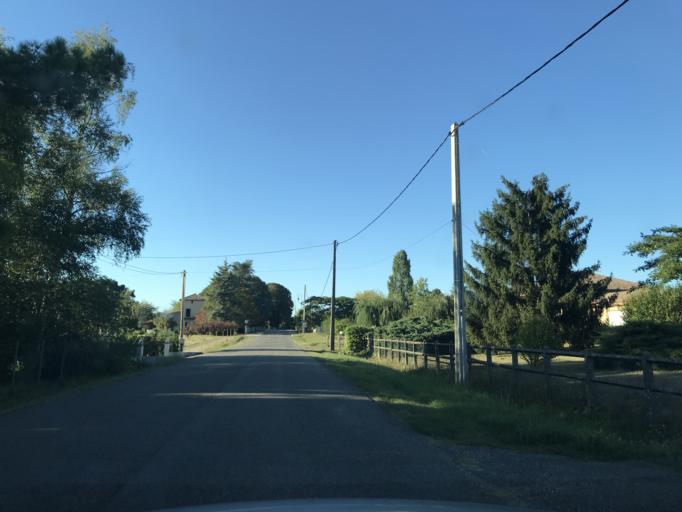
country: FR
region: Aquitaine
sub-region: Departement de la Gironde
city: Sauveterre-de-Guyenne
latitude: 44.7457
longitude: -0.0723
